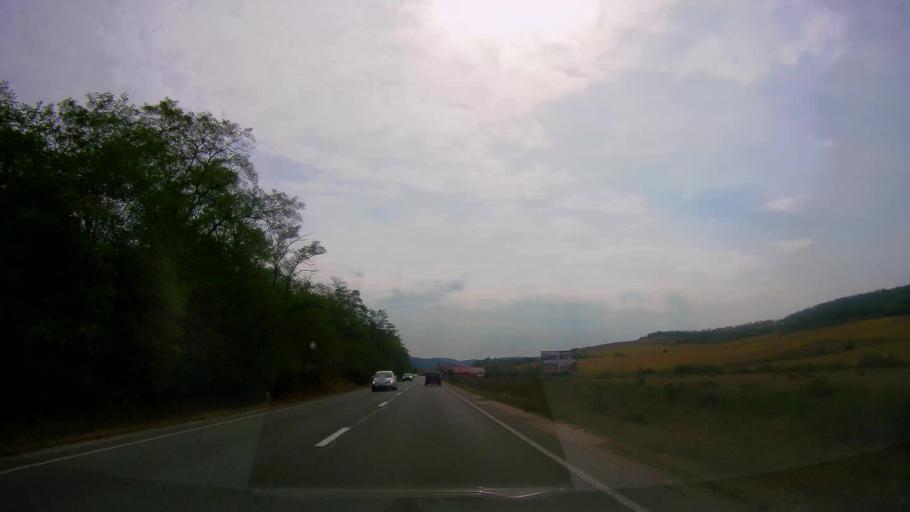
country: RO
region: Salaj
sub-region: Comuna Hida
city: Hida
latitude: 47.0501
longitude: 23.2407
